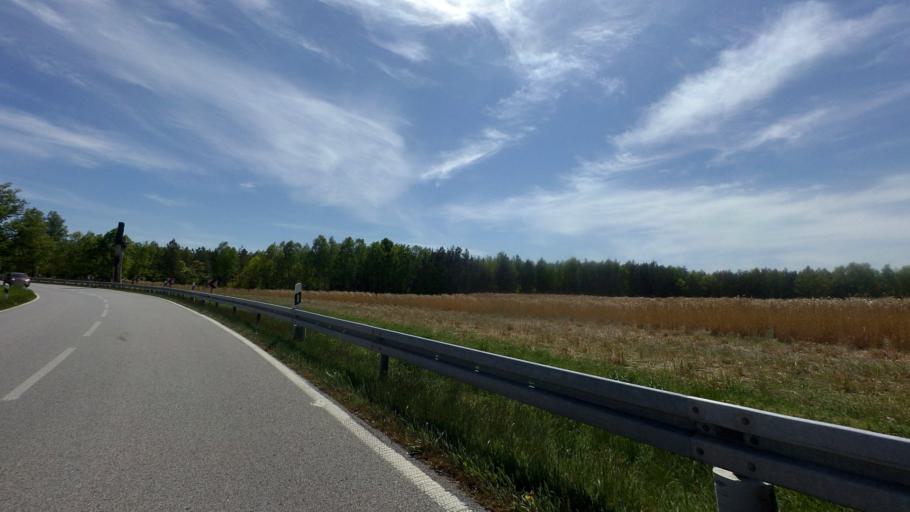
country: DE
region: Brandenburg
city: Baruth
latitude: 52.0483
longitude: 13.4396
